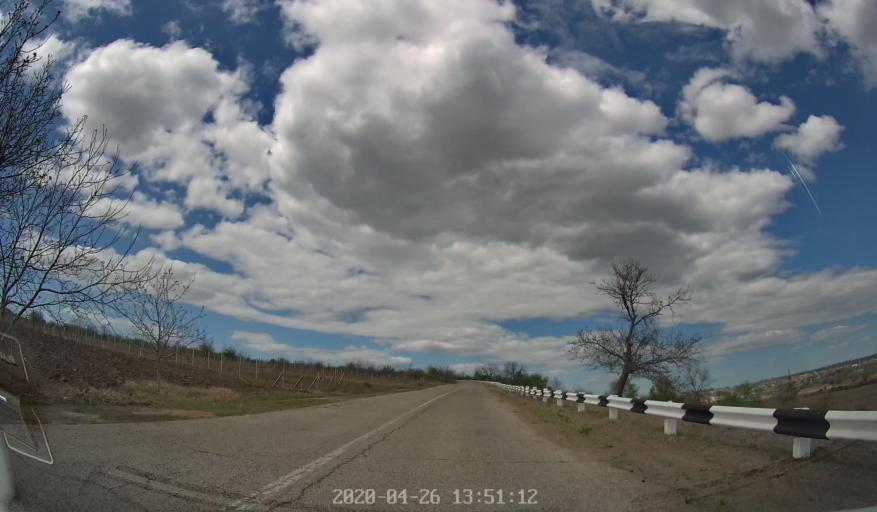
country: MD
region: Telenesti
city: Dubasari
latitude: 47.2653
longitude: 29.1257
